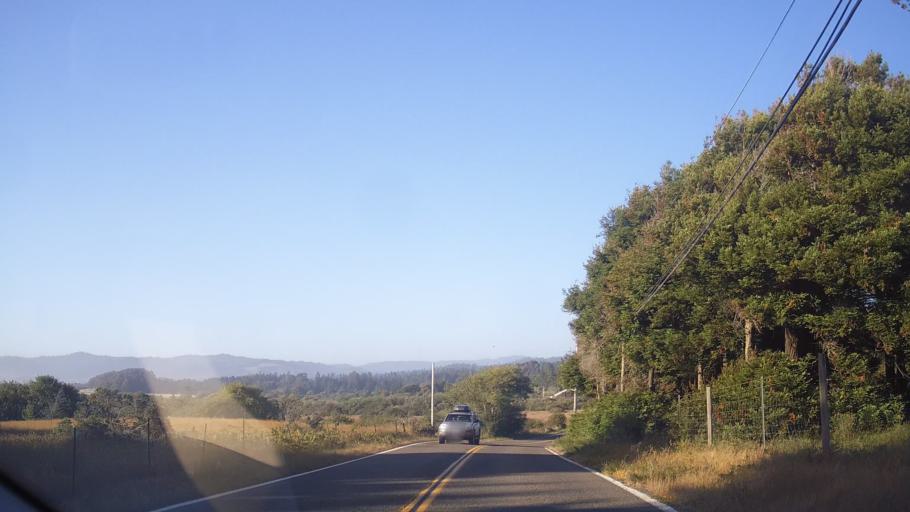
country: US
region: California
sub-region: Mendocino County
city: Fort Bragg
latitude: 39.5029
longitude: -123.7715
